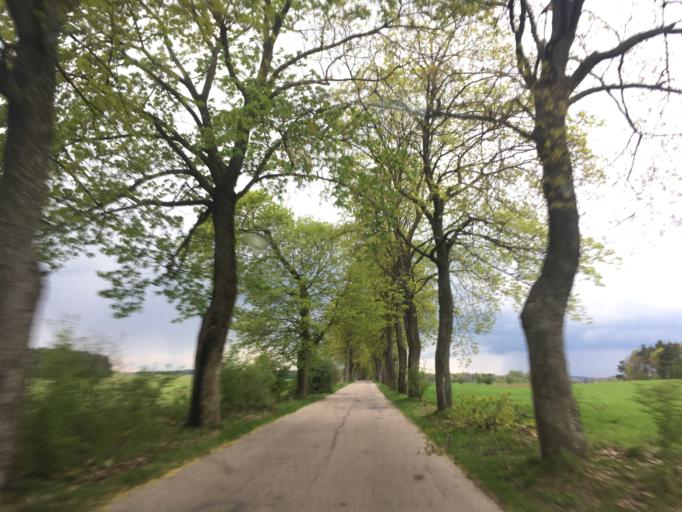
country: PL
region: Warmian-Masurian Voivodeship
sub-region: Powiat ostrodzki
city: Dabrowno
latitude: 53.4130
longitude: 20.1098
